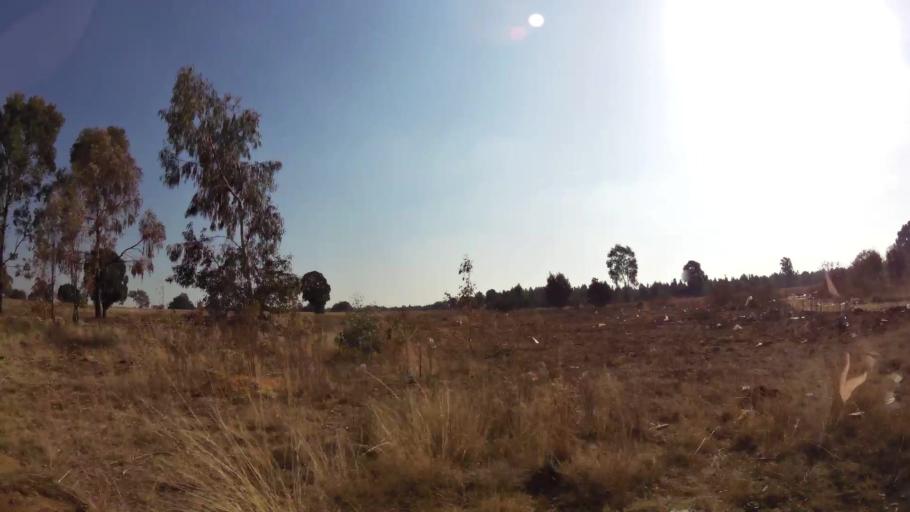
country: ZA
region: Gauteng
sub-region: West Rand District Municipality
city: Randfontein
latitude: -26.1810
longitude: 27.6782
